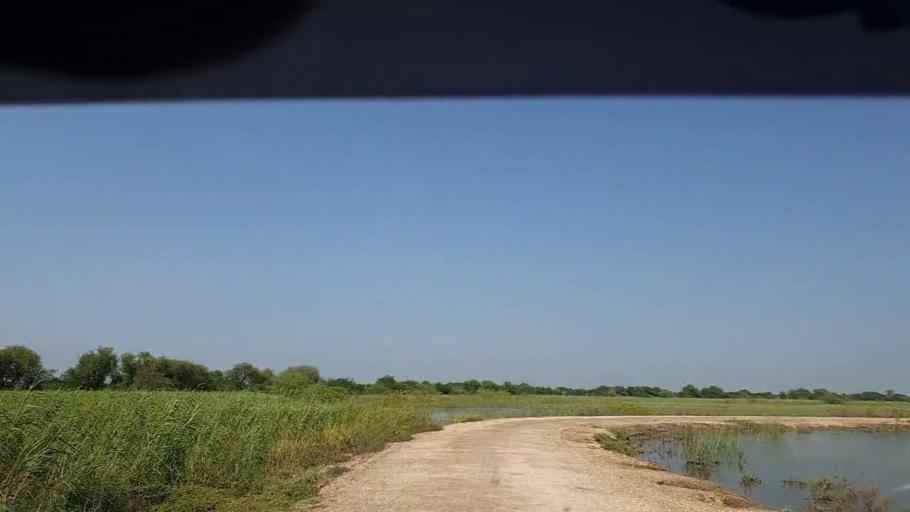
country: PK
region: Sindh
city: Badin
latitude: 24.4606
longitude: 68.7680
